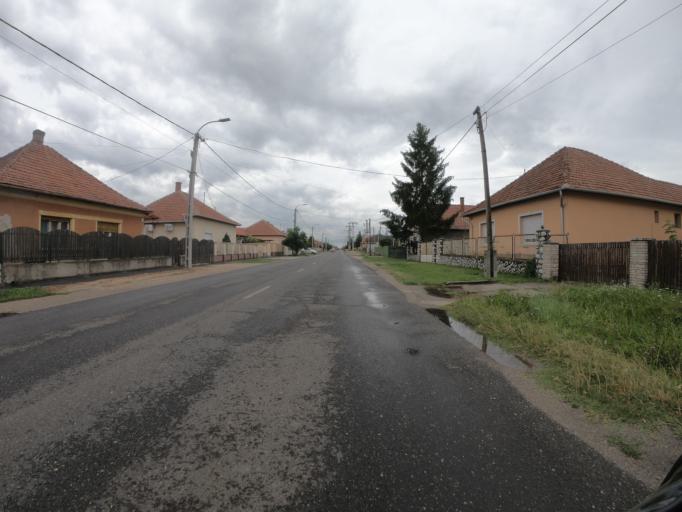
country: HU
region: Borsod-Abauj-Zemplen
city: Mezokovesd
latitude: 47.8120
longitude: 20.5833
